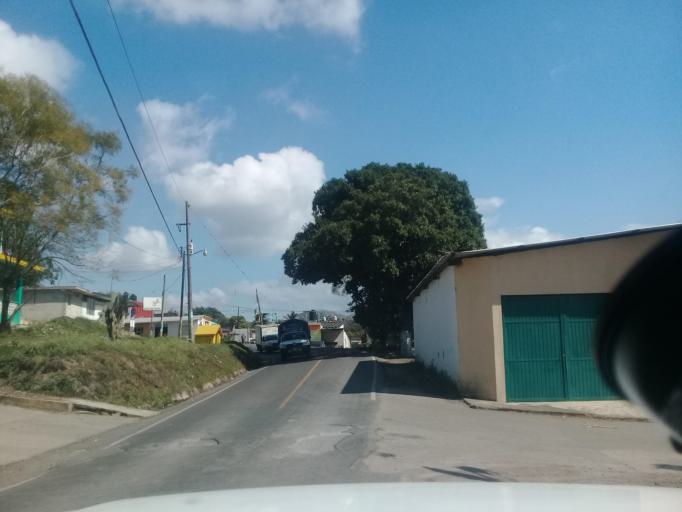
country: MX
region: Veracruz
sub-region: Coatepec
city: Bella Esperanza
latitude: 19.4328
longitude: -96.8678
